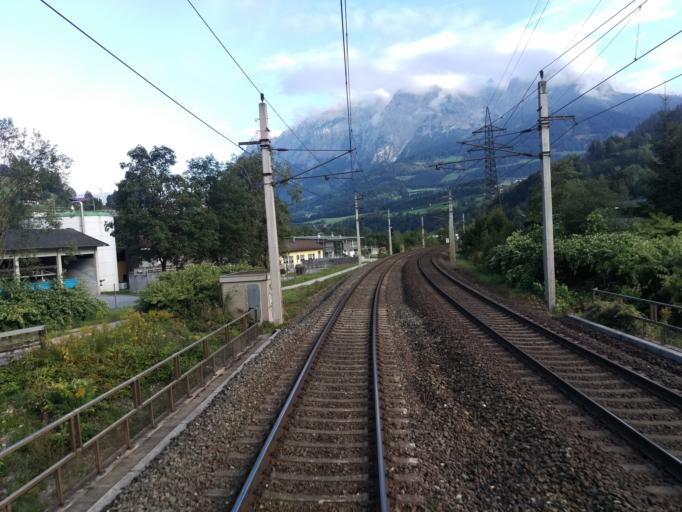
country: AT
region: Salzburg
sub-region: Politischer Bezirk Sankt Johann im Pongau
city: Pfarrwerfen
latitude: 47.4372
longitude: 13.2116
